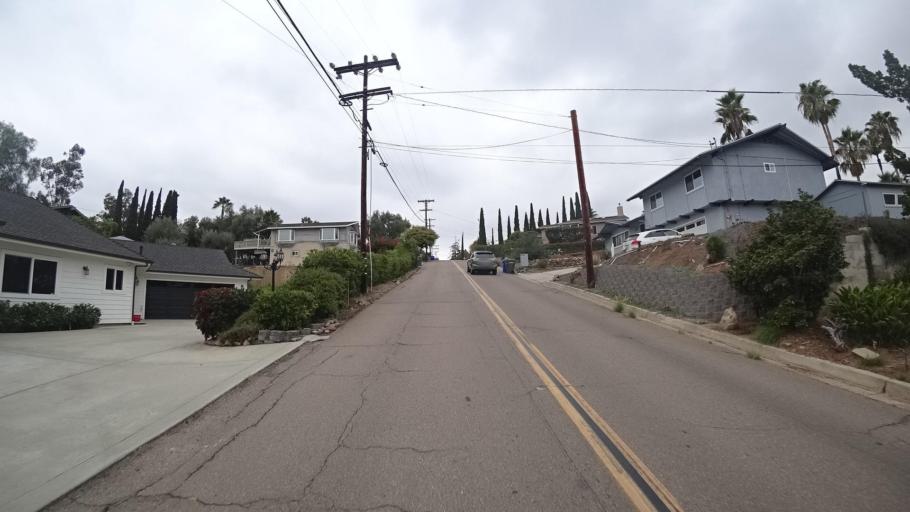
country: US
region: California
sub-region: San Diego County
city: Casa de Oro-Mount Helix
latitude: 32.7588
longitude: -116.9756
